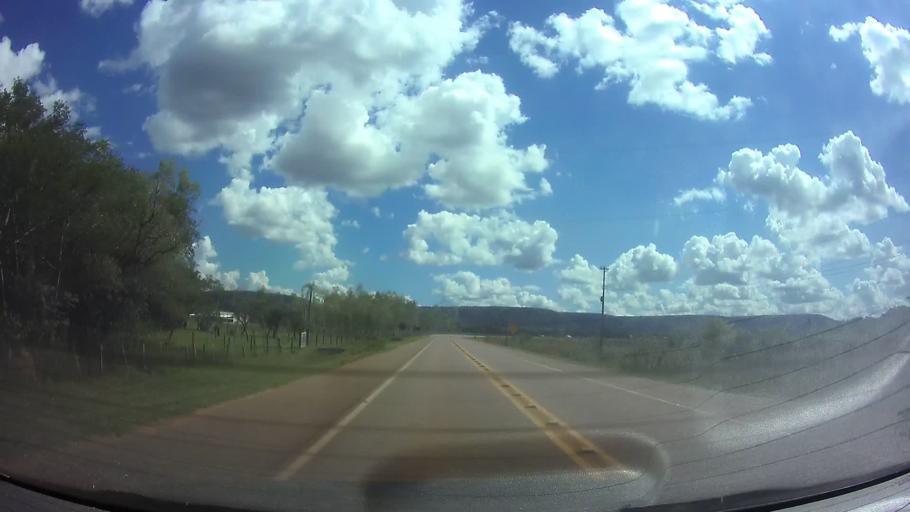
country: PY
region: Guaira
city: Itape
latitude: -25.9111
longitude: -56.6767
